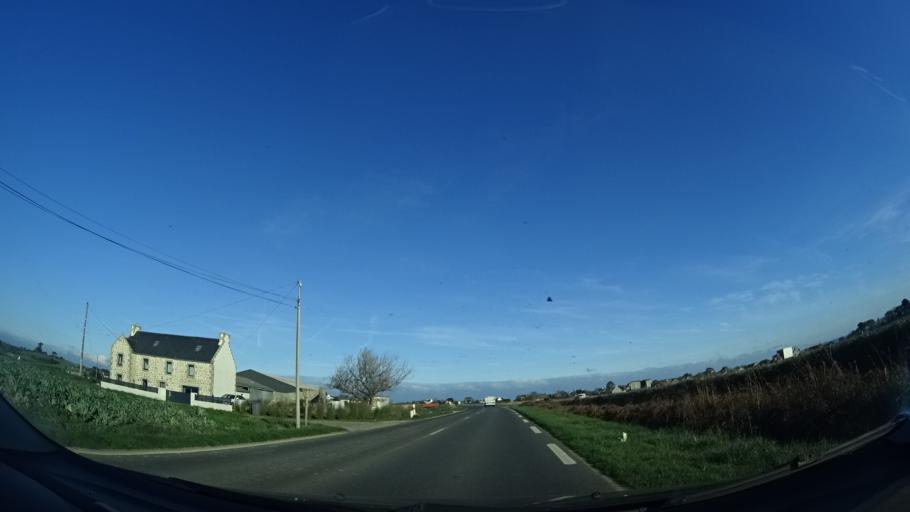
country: FR
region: Brittany
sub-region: Departement du Finistere
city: Saint-Pol-de-Leon
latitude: 48.6981
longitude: -3.9943
